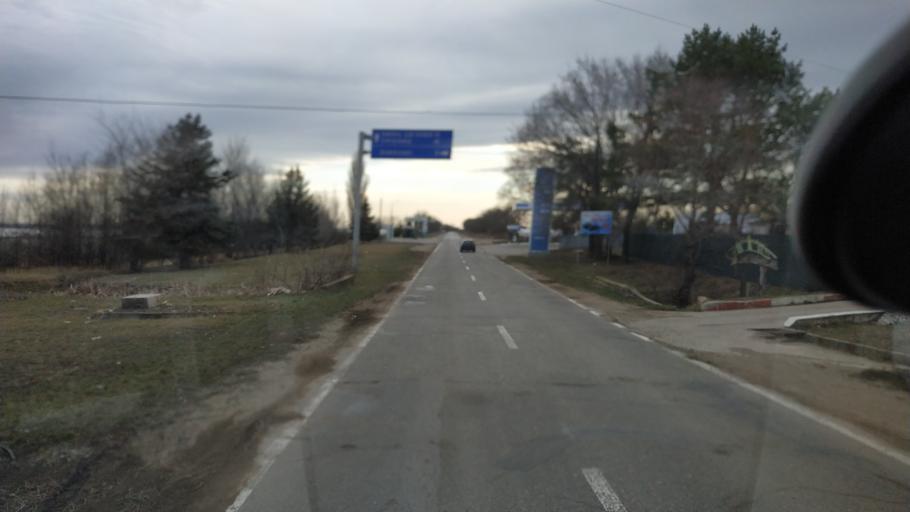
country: MD
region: Criuleni
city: Criuleni
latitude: 47.2007
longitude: 29.1536
